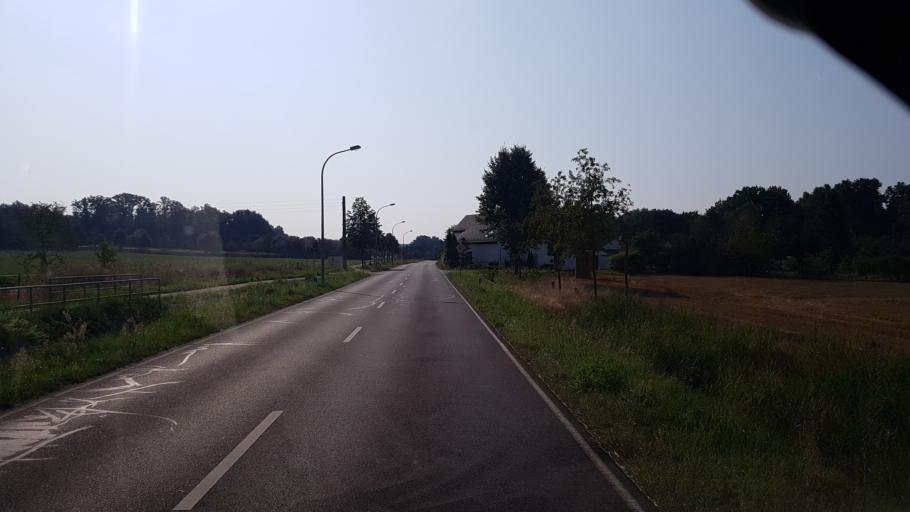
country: DE
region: Brandenburg
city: Drebkau
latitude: 51.6935
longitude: 14.2643
